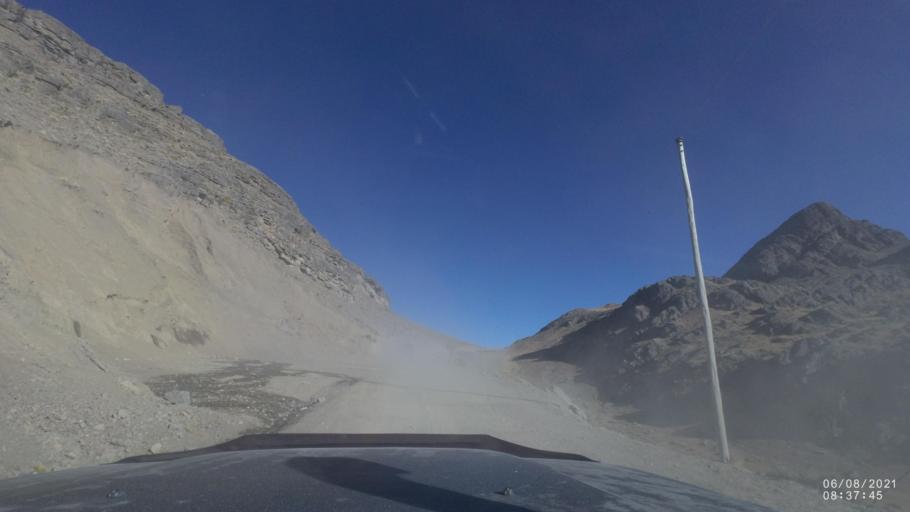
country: BO
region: Cochabamba
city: Sipe Sipe
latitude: -17.1748
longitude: -66.3908
